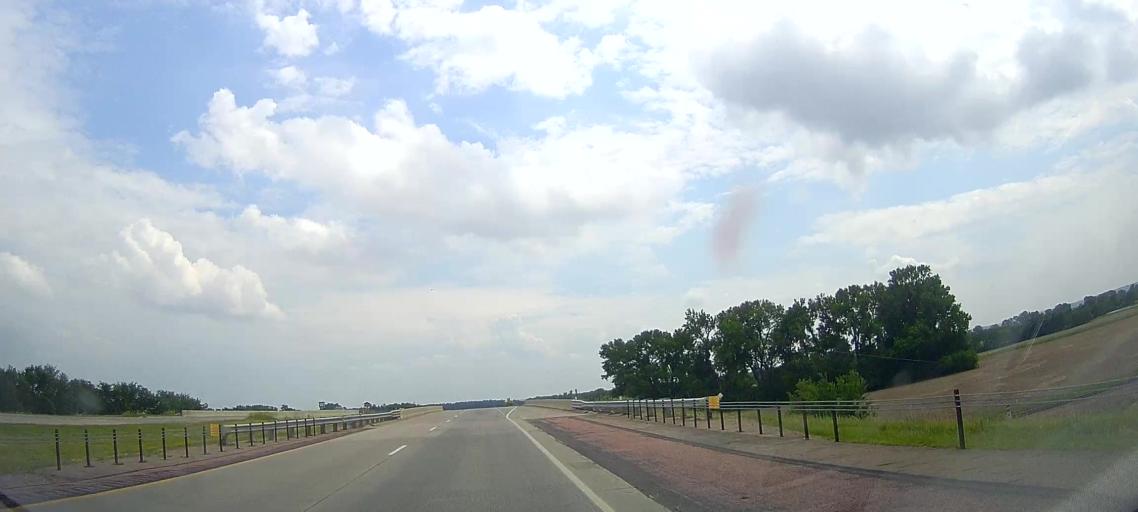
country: US
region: South Dakota
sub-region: Union County
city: Elk Point
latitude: 42.6949
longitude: -96.6974
